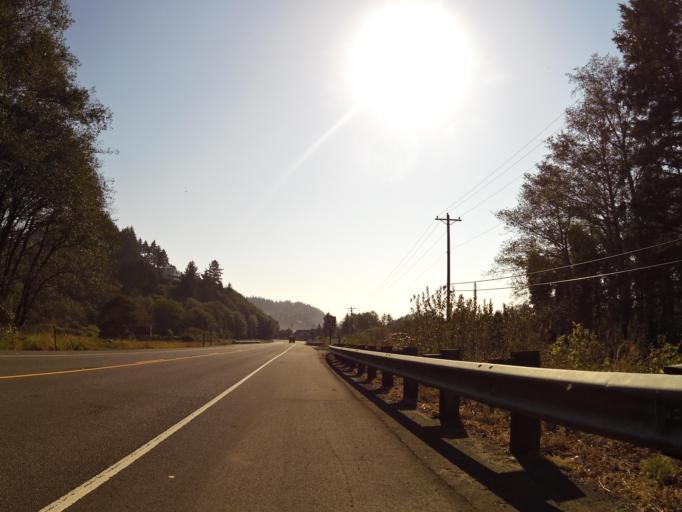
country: US
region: Oregon
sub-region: Tillamook County
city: Pacific City
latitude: 45.1058
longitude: -123.9785
